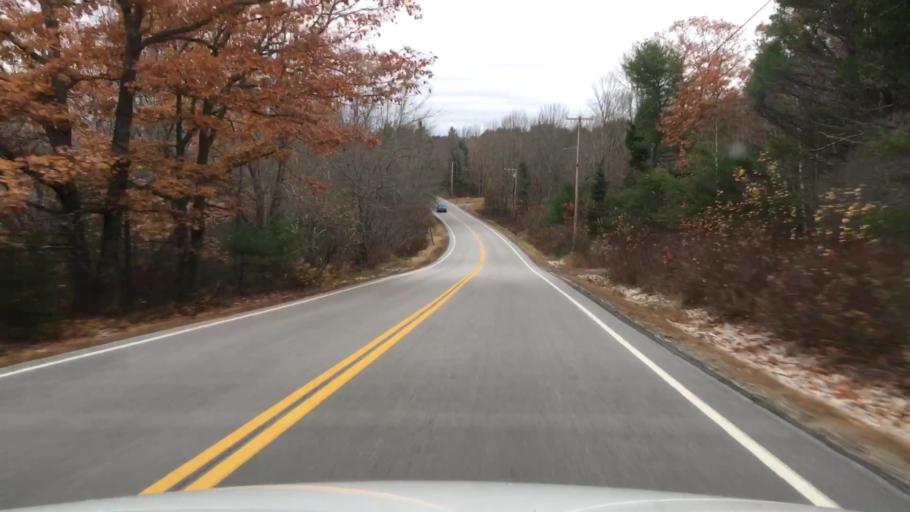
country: US
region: Maine
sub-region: Hancock County
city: Orland
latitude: 44.5374
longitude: -68.6800
